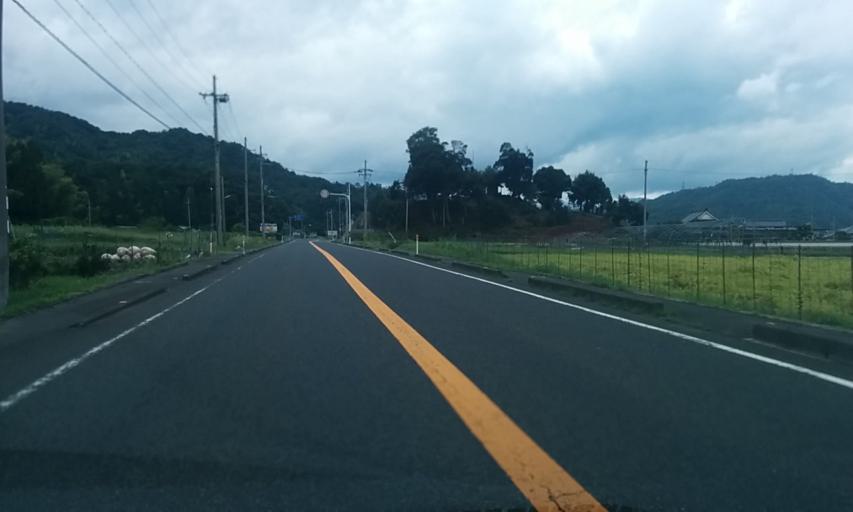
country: JP
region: Kyoto
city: Miyazu
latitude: 35.5384
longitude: 135.2377
